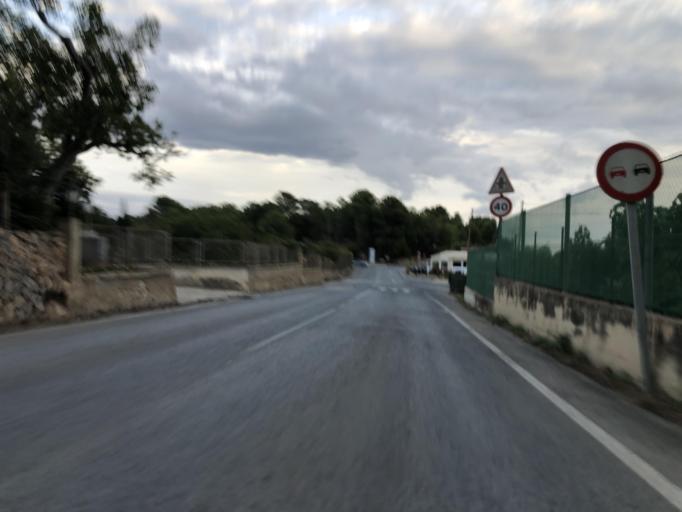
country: ES
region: Valencia
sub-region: Provincia de Alicante
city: Polop
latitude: 38.6261
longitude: -0.1372
